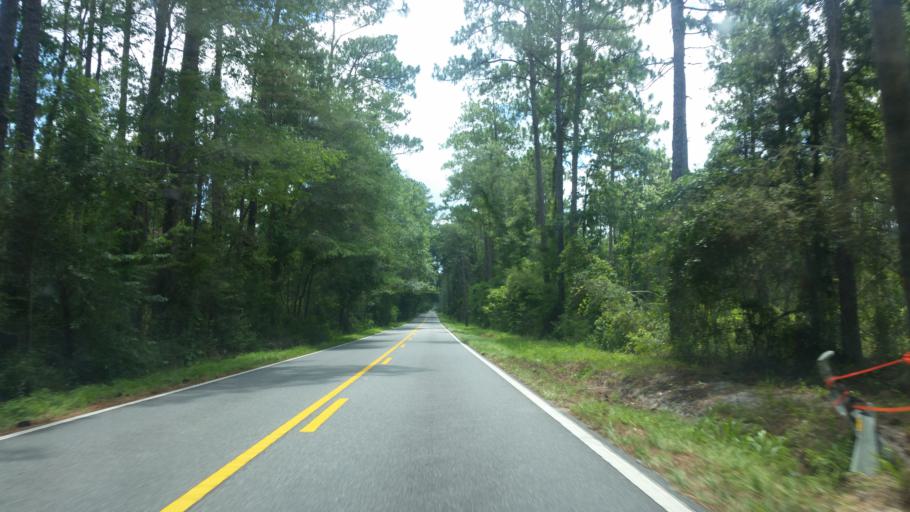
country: US
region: Florida
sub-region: Leon County
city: Woodville
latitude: 30.2994
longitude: -84.2102
